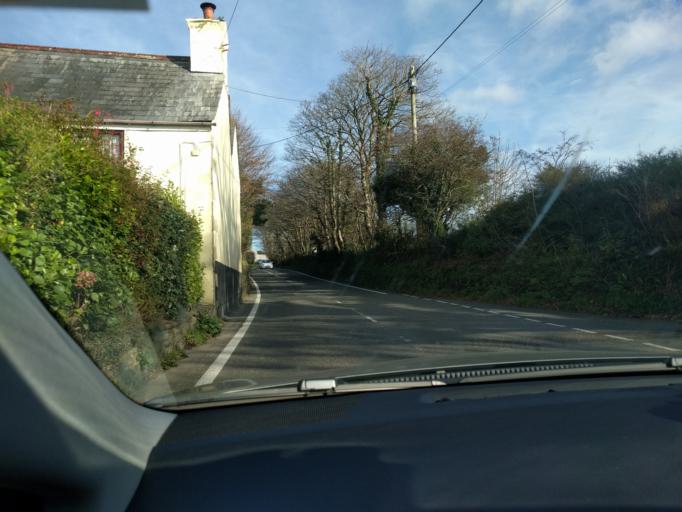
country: GB
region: England
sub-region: Cornwall
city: Camelford
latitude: 50.6251
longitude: -4.6709
